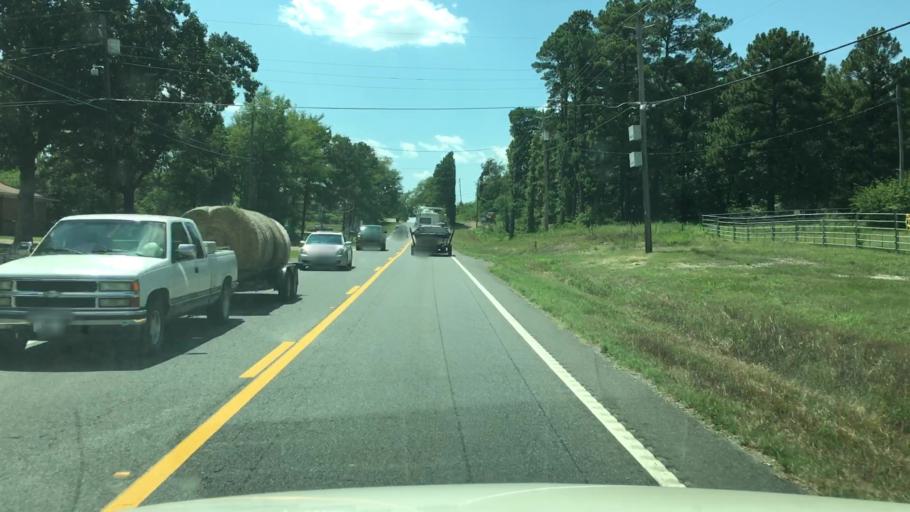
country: US
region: Arkansas
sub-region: Garland County
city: Piney
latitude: 34.5096
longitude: -93.1545
